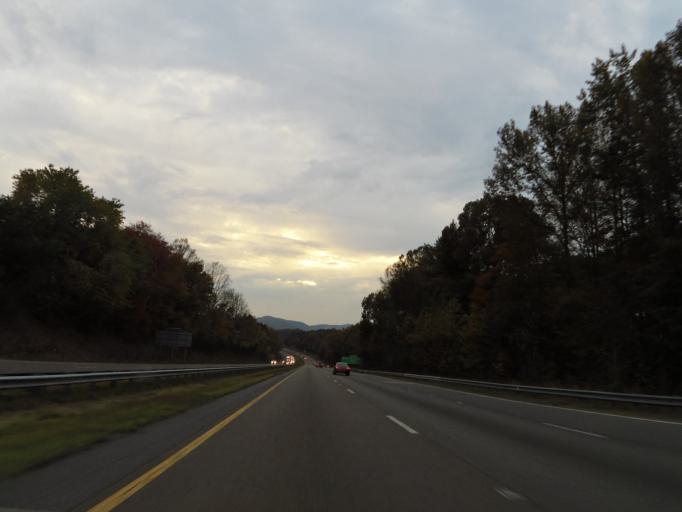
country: US
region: North Carolina
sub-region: Burke County
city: Rutherford College
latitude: 35.7332
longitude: -81.5338
